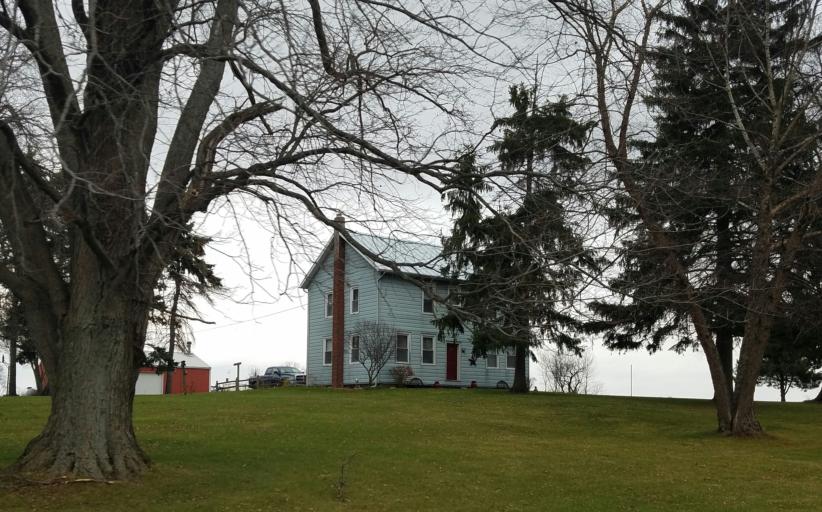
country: US
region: Ohio
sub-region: Crawford County
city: Galion
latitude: 40.6982
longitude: -82.8758
